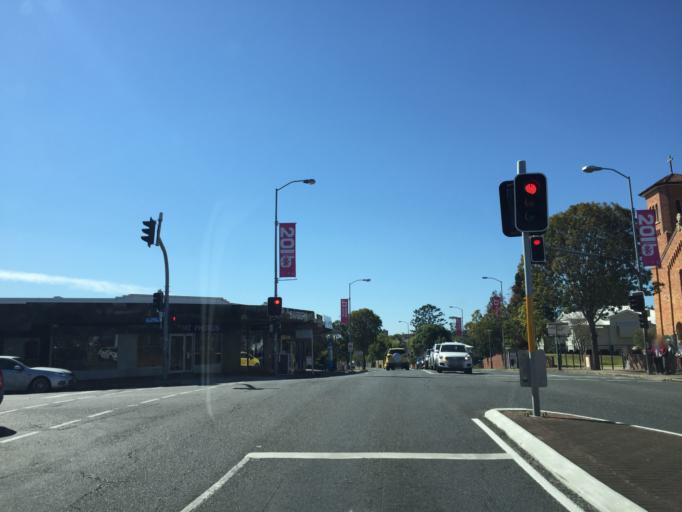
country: AU
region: Queensland
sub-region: Brisbane
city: Milton
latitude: -27.4454
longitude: 152.9937
